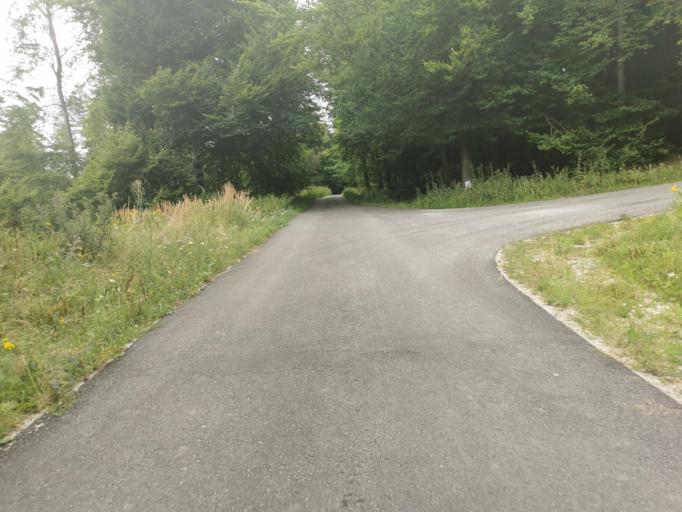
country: SK
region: Trenciansky
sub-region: Okres Myjava
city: Myjava
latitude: 48.8241
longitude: 17.6082
